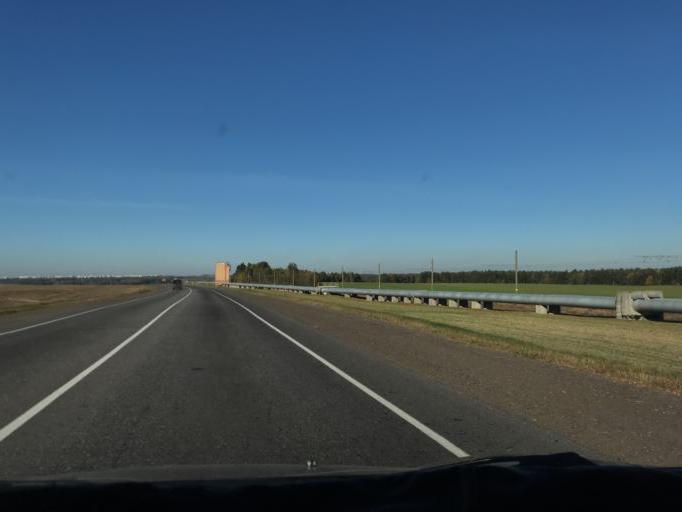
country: BY
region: Gomel
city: Mazyr
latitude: 51.9672
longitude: 29.2618
